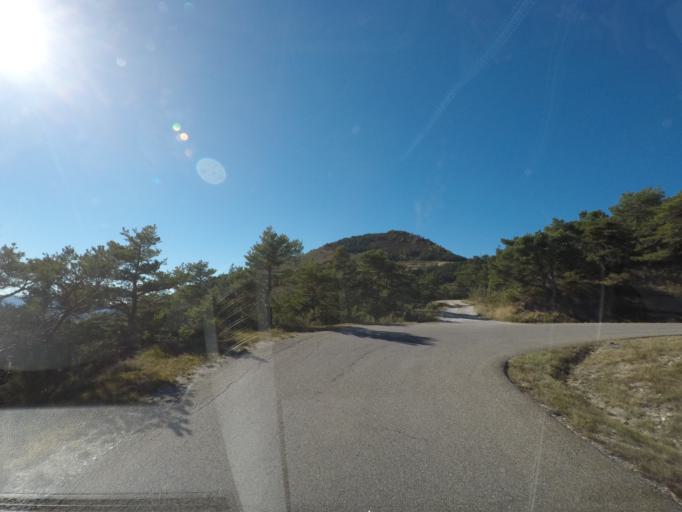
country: FR
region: Provence-Alpes-Cote d'Azur
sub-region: Departement des Hautes-Alpes
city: Serres
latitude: 44.4294
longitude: 5.5769
